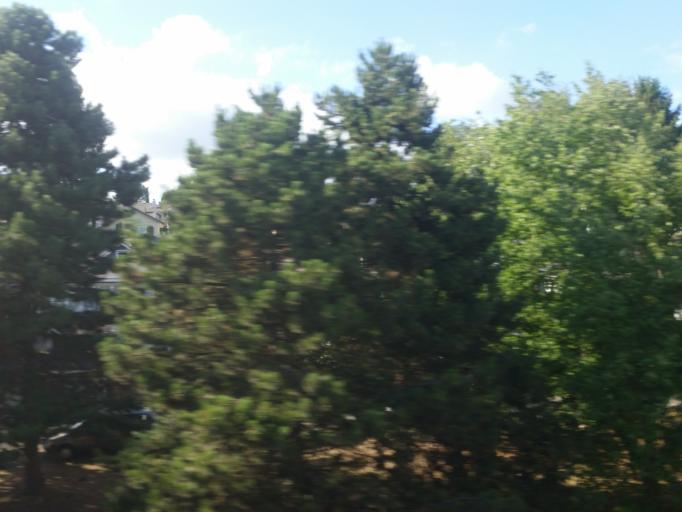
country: CA
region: British Columbia
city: New Westminster
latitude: 49.2029
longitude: -122.9378
